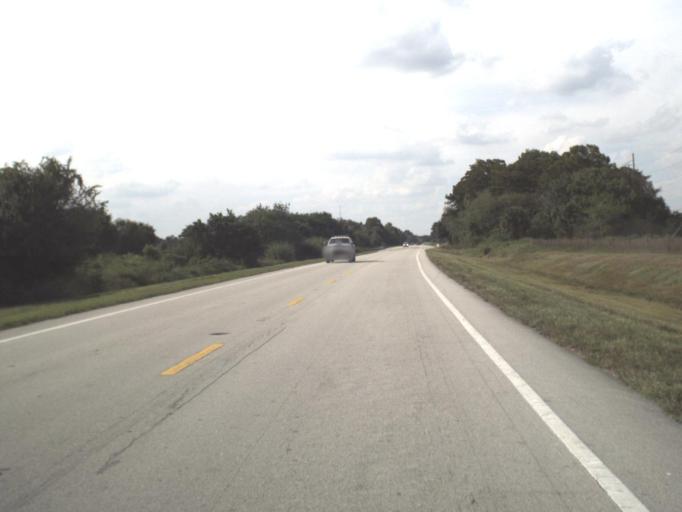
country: US
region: Florida
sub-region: Okeechobee County
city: Taylor Creek
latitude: 27.2025
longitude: -80.7430
